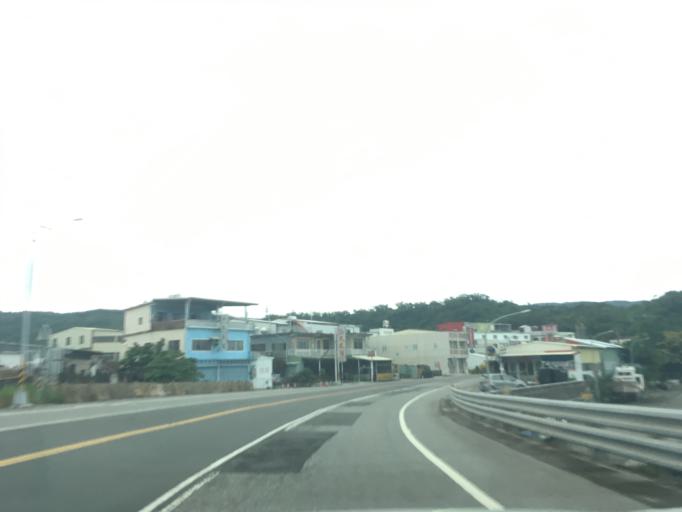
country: TW
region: Taiwan
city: Hengchun
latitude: 22.3382
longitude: 120.8935
